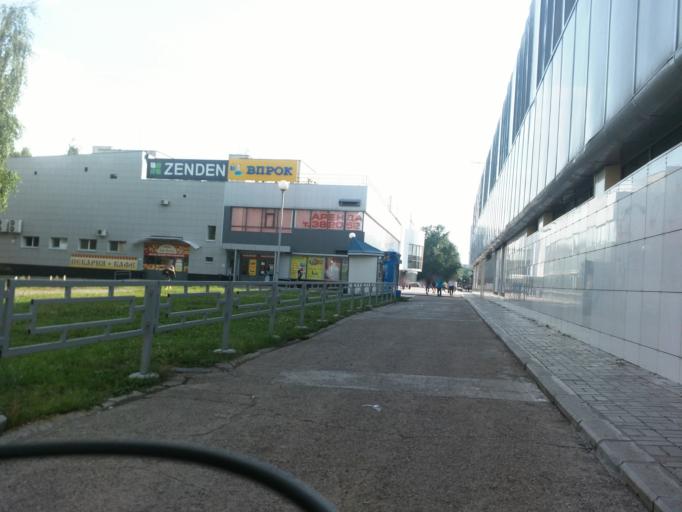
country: RU
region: Tatarstan
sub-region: Tukayevskiy Rayon
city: Naberezhnyye Chelny
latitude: 55.7447
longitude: 52.4219
